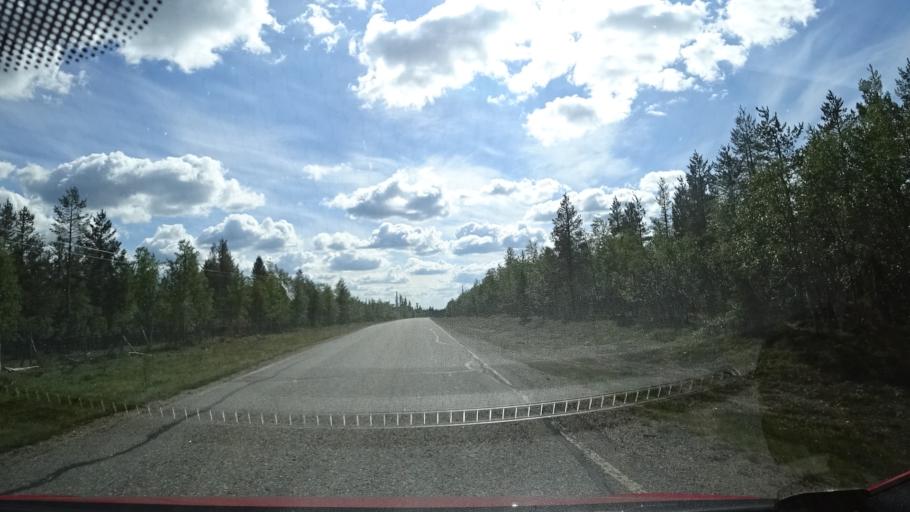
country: FI
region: Lapland
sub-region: Pohjois-Lappi
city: Inari
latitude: 68.5053
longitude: 26.1048
